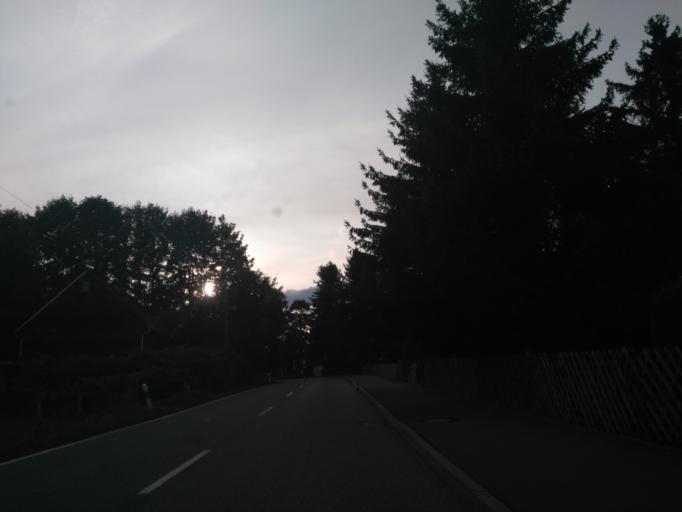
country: DE
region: Saxony
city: Geyer
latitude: 50.6262
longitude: 12.9320
